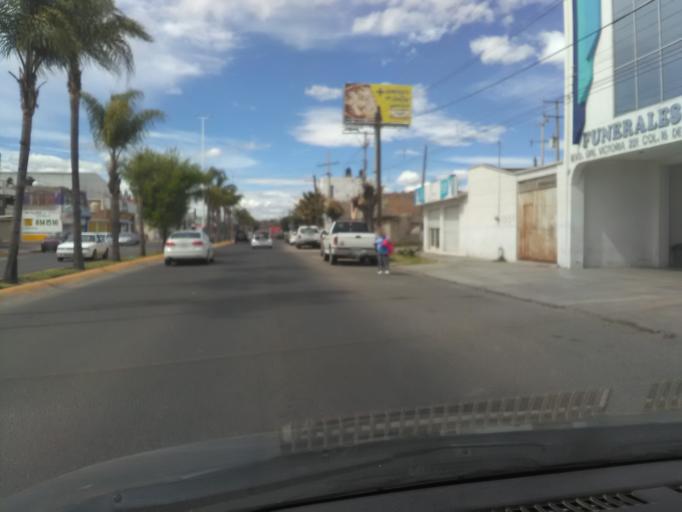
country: MX
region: Durango
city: Victoria de Durango
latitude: 24.0391
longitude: -104.6661
